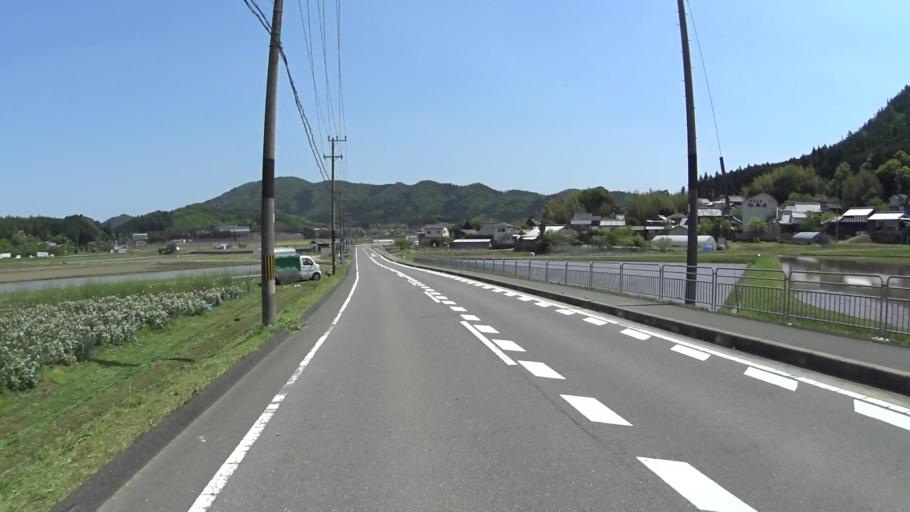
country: JP
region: Kyoto
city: Kameoka
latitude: 35.0268
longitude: 135.4863
